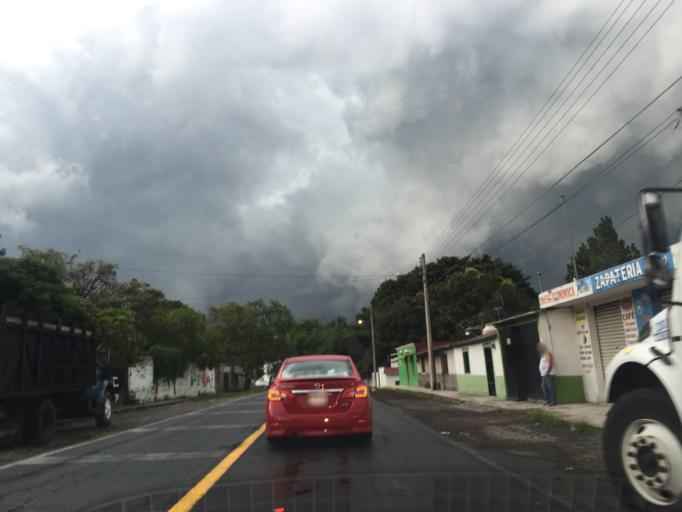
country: MX
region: Colima
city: Queseria
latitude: 19.3632
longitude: -103.5779
